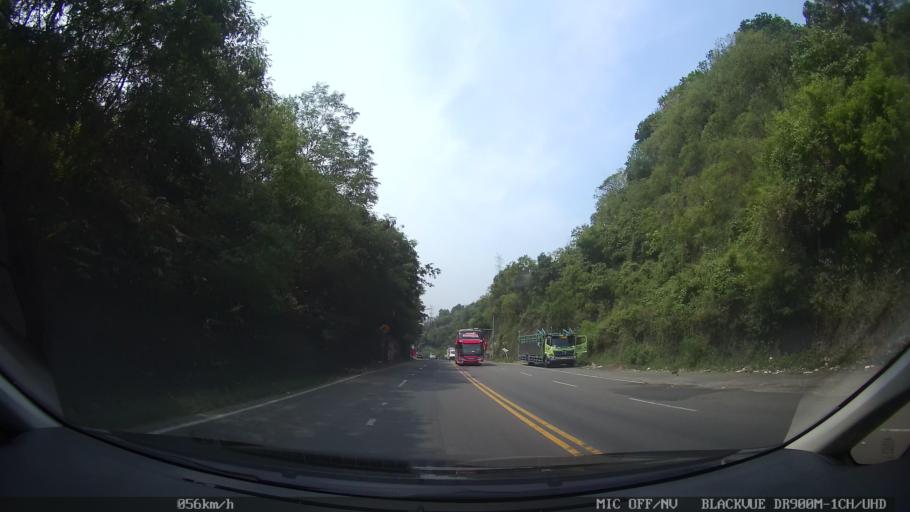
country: ID
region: Banten
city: Curug
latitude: -5.9497
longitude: 106.0023
